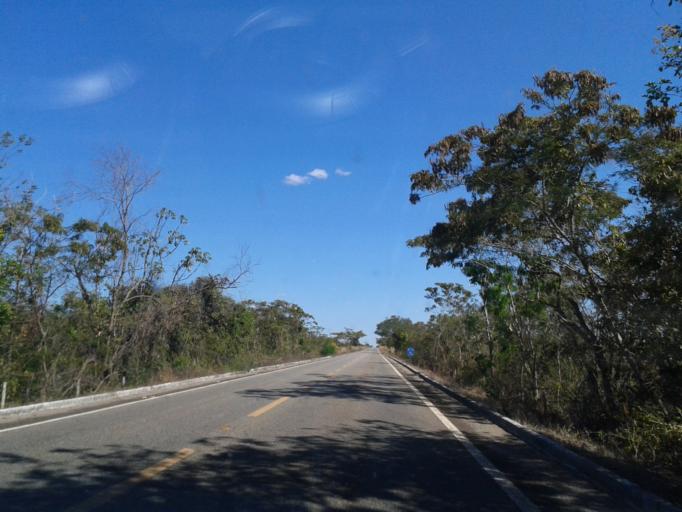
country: BR
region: Goias
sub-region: Sao Miguel Do Araguaia
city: Sao Miguel do Araguaia
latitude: -13.6347
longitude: -50.3133
